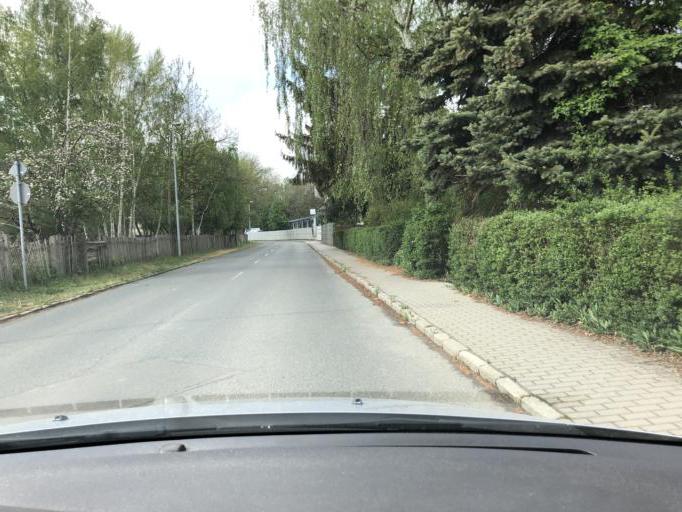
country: DE
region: Thuringia
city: Altenburg
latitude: 51.0061
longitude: 12.4415
